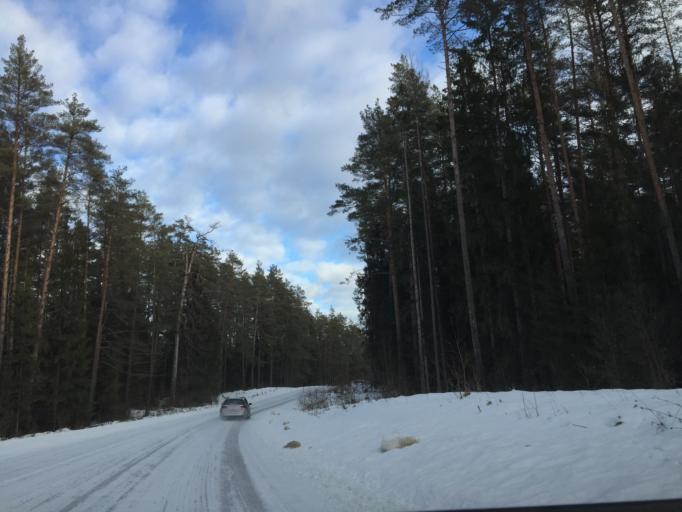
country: LV
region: Ogre
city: Jumprava
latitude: 56.5594
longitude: 24.9040
